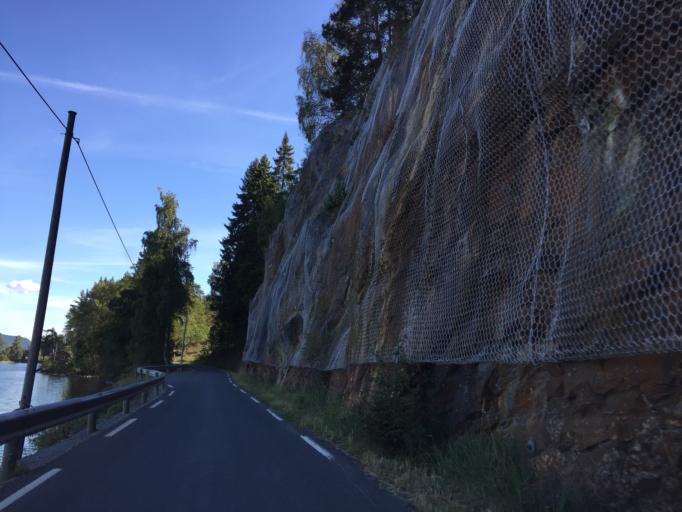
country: NO
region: Buskerud
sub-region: Ovre Eiker
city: Hokksund
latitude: 59.6787
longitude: 9.8628
